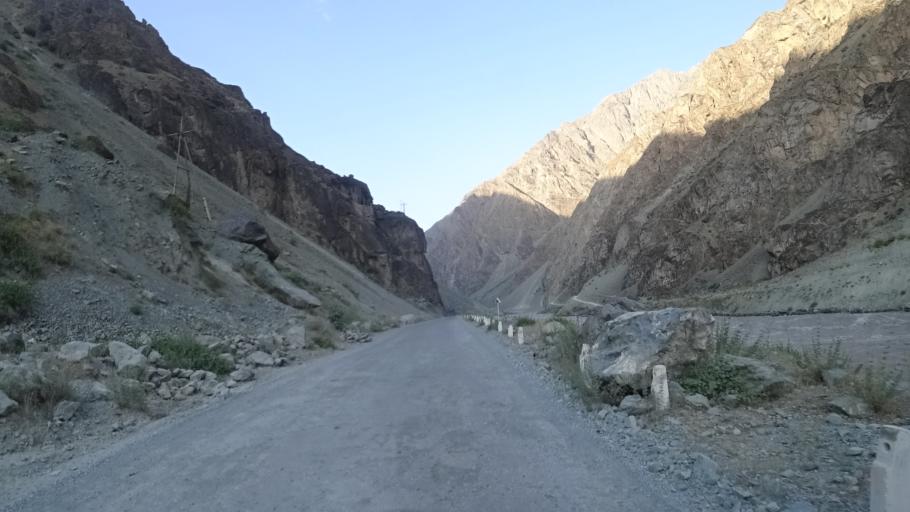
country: TJ
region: Gorno-Badakhshan
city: Qalaikhumb
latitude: 38.4215
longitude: 70.7425
